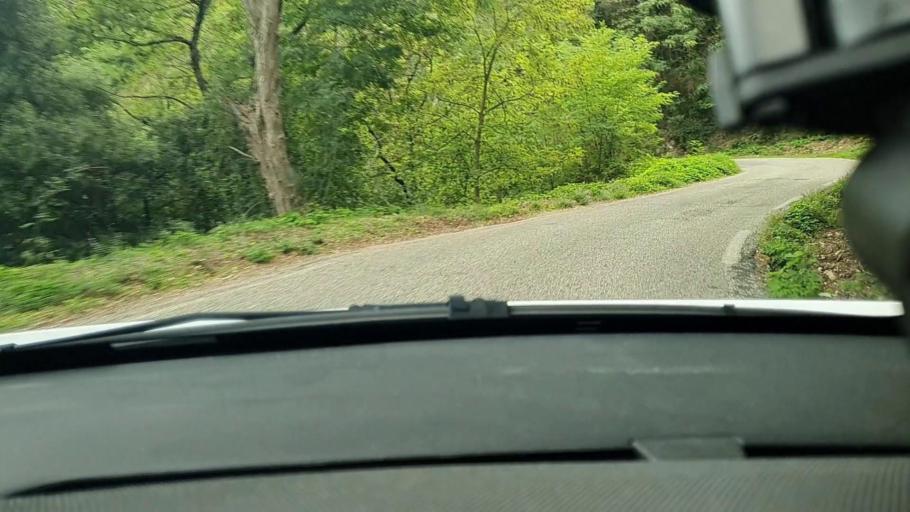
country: FR
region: Languedoc-Roussillon
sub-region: Departement du Gard
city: Branoux-les-Taillades
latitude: 44.2991
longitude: 3.9896
